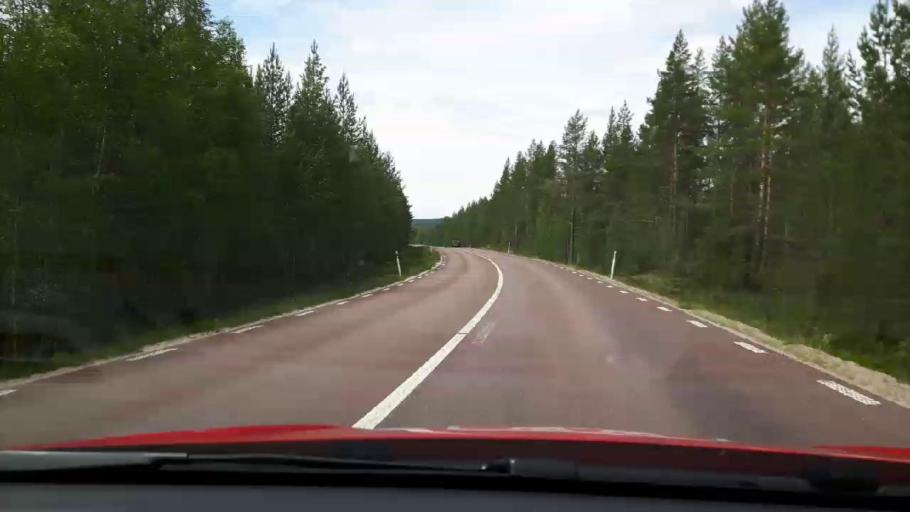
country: SE
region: Jaemtland
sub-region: Harjedalens Kommun
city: Sveg
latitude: 62.0586
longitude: 14.5871
